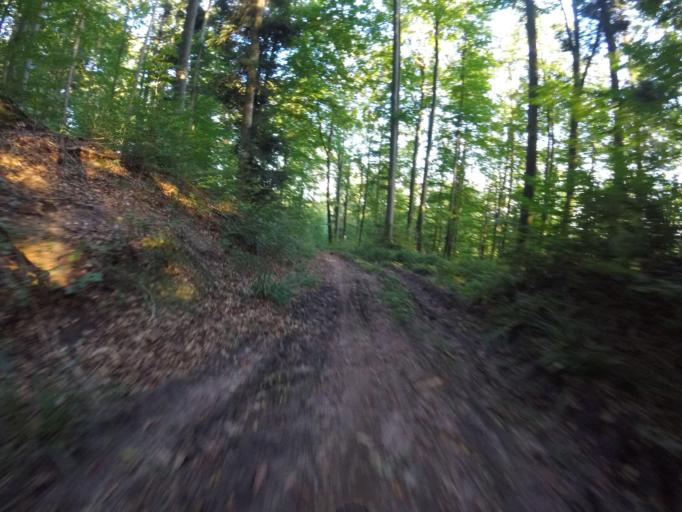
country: DE
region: Baden-Wuerttemberg
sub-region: Regierungsbezirk Stuttgart
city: Spiegelberg
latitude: 49.0077
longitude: 9.4281
